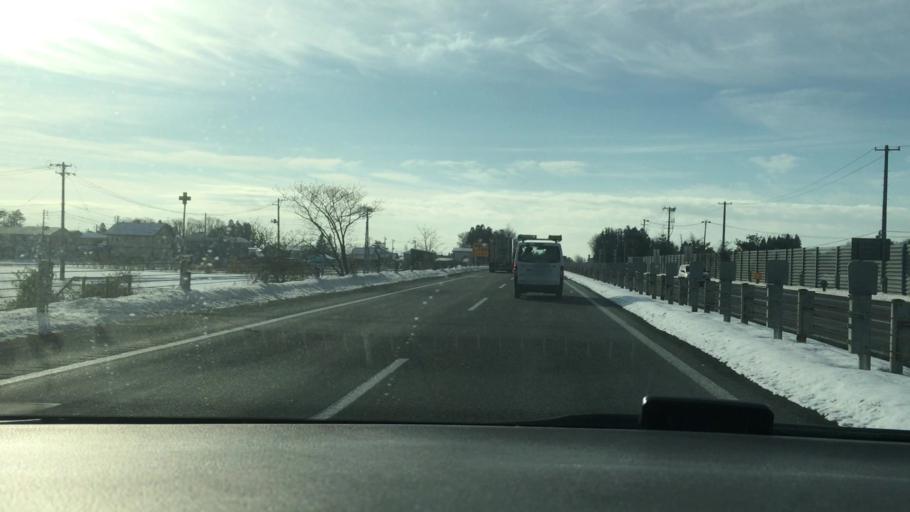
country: JP
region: Iwate
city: Hanamaki
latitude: 39.4010
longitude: 141.0925
